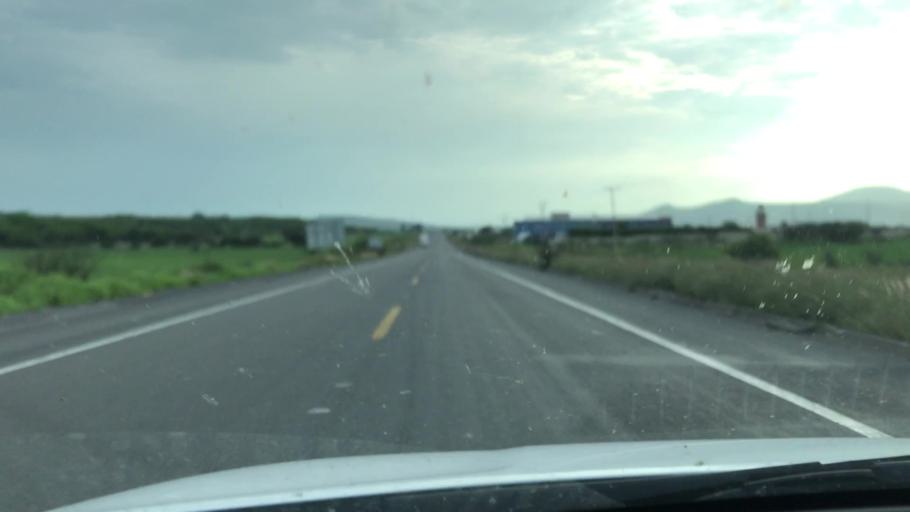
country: MX
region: Jalisco
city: Degollado
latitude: 20.3644
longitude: -102.1381
